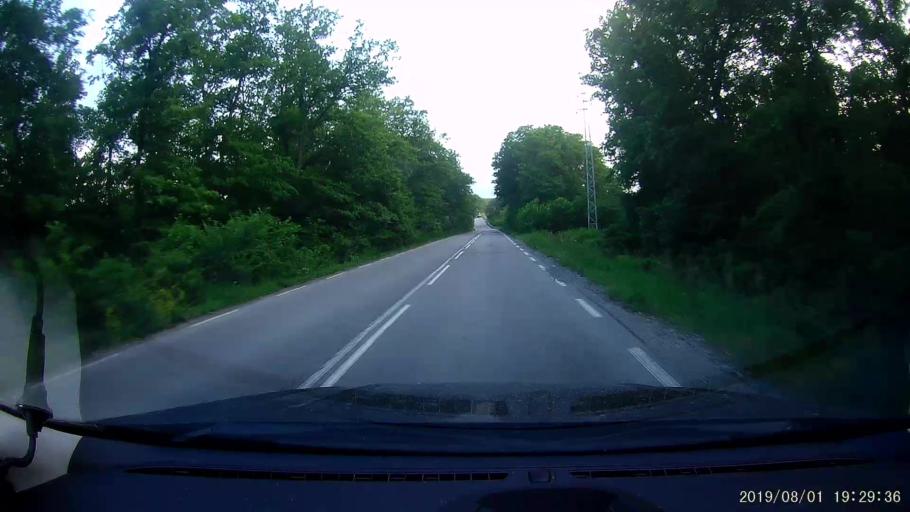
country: BG
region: Burgas
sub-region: Obshtina Sungurlare
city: Sungurlare
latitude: 42.8237
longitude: 26.9053
